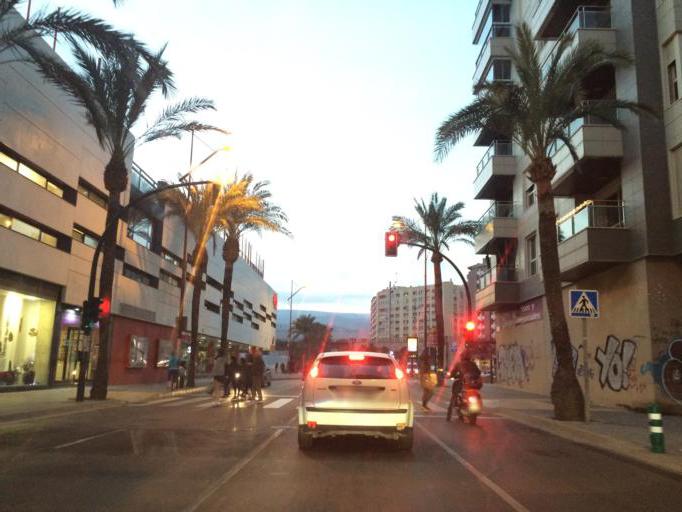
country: ES
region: Andalusia
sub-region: Provincia de Almeria
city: Almeria
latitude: 36.8325
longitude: -2.4594
